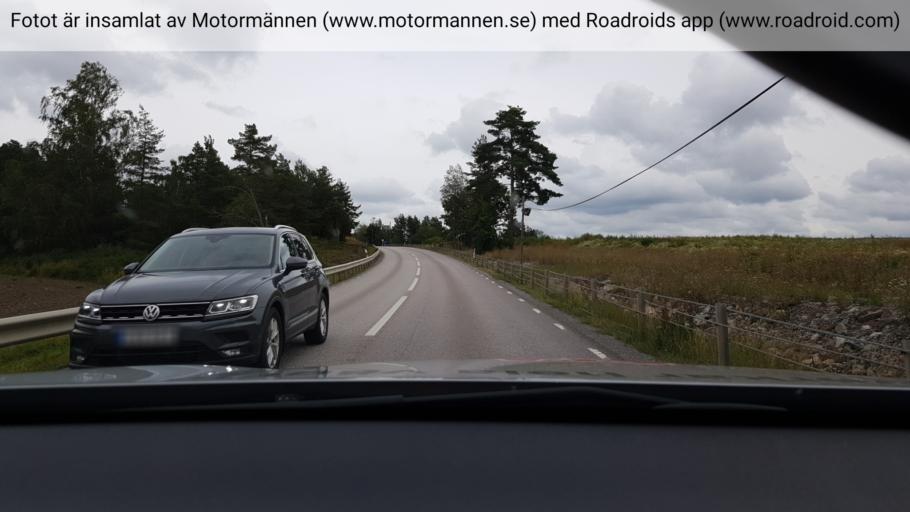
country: SE
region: Stockholm
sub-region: Sigtuna Kommun
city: Sigtuna
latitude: 59.6462
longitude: 17.6307
